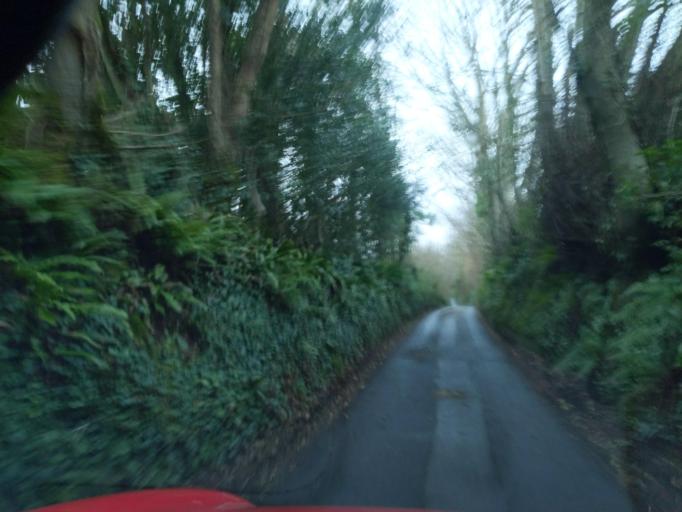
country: GB
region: England
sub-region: Devon
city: Wembury
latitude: 50.3259
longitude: -4.0762
